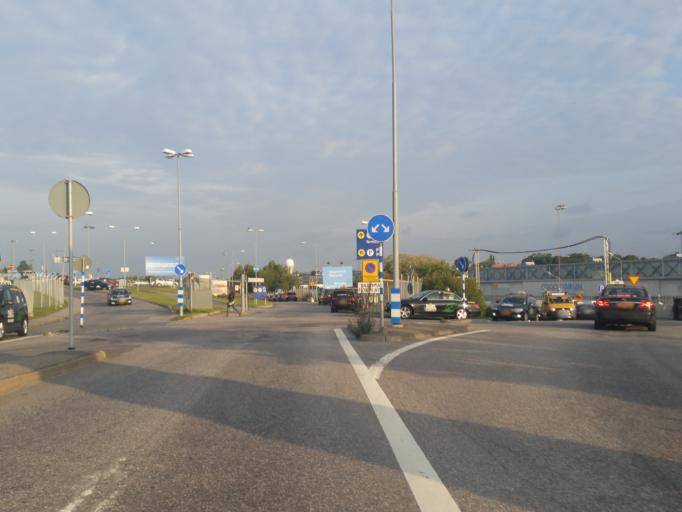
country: SE
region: Stockholm
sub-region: Sundbybergs Kommun
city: Sundbyberg
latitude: 59.3541
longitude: 17.9544
